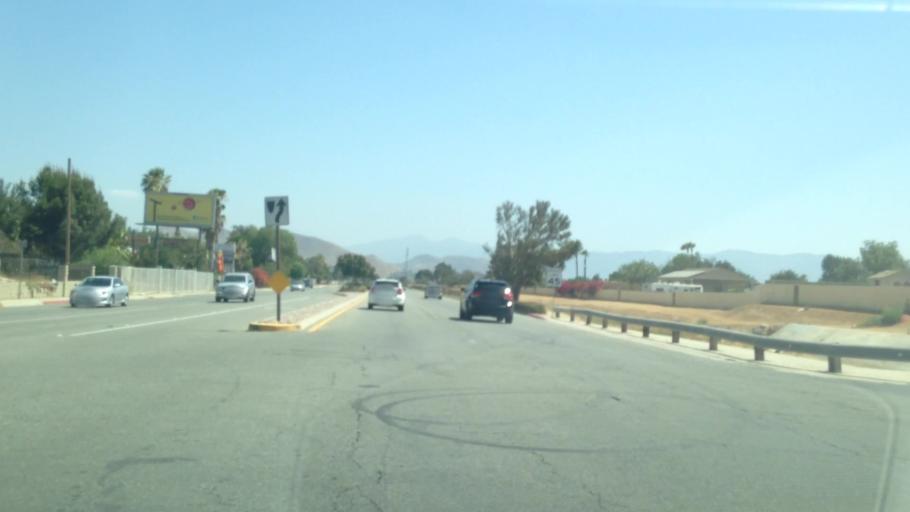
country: US
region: California
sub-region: Riverside County
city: Mira Loma
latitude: 33.9901
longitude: -117.5234
